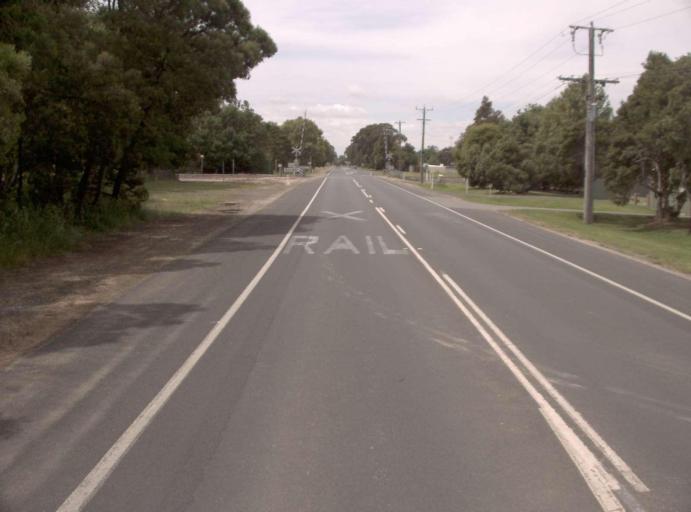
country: AU
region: Victoria
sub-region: Wellington
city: Sale
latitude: -38.0875
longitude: 147.0606
